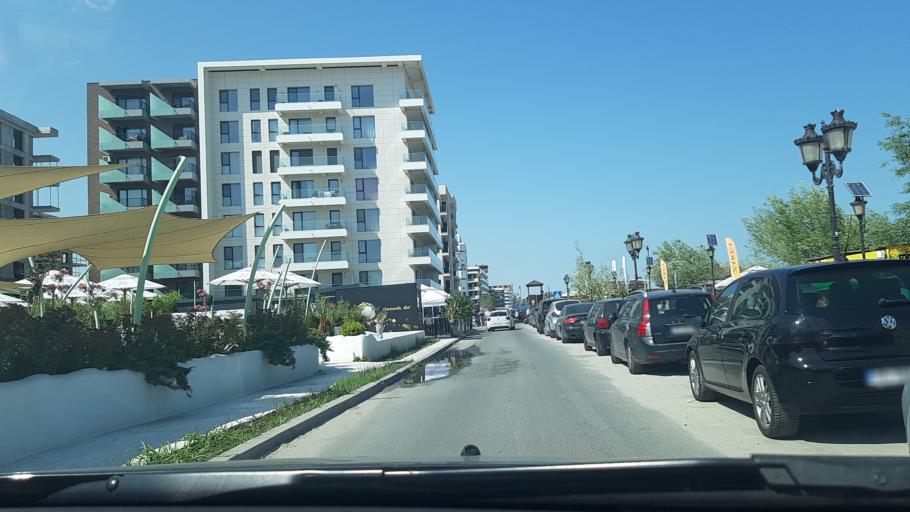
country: RO
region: Constanta
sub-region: Comuna Navodari
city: Navodari
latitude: 44.3041
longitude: 28.6275
